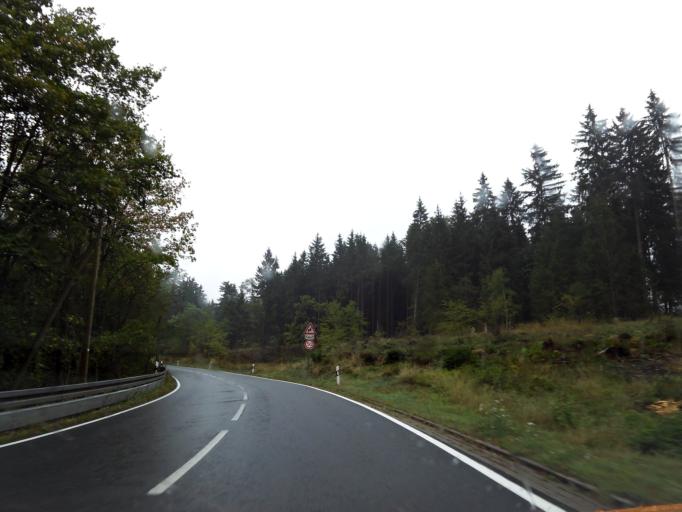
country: DE
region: Saxony-Anhalt
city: Stolberg
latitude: 51.6475
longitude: 10.9220
